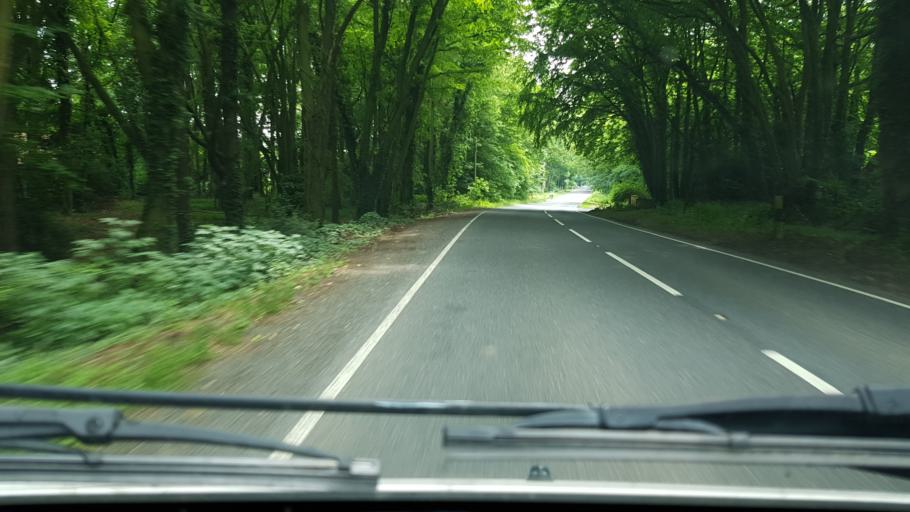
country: GB
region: England
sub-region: Gloucestershire
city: Donnington
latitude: 51.9829
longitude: -1.7674
